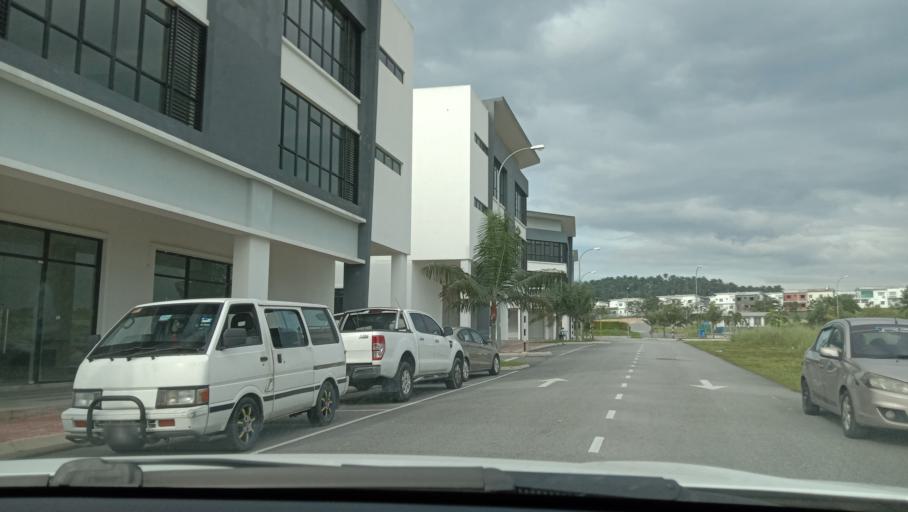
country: MY
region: Selangor
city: Ladang Seri Kundang
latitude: 3.2420
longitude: 101.4755
